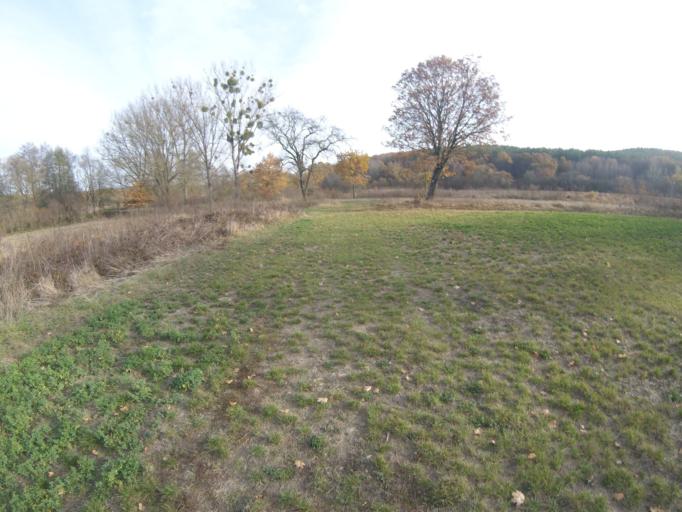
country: HU
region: Borsod-Abauj-Zemplen
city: Gonc
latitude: 48.4909
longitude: 21.4617
